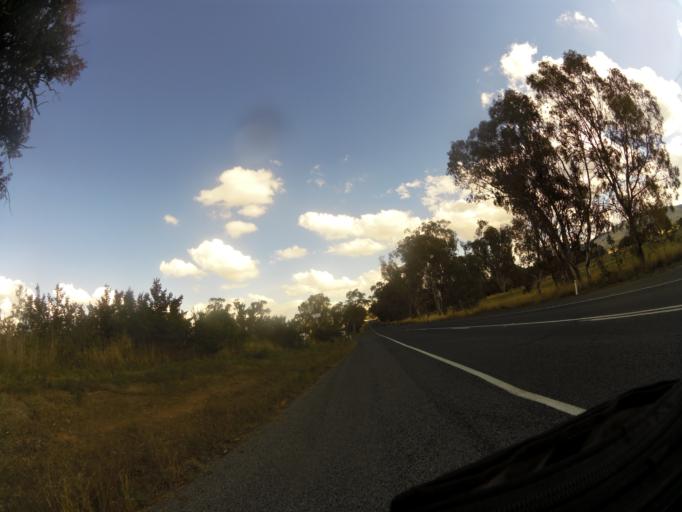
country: AU
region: Victoria
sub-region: Mansfield
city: Mansfield
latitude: -36.9328
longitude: 146.0001
